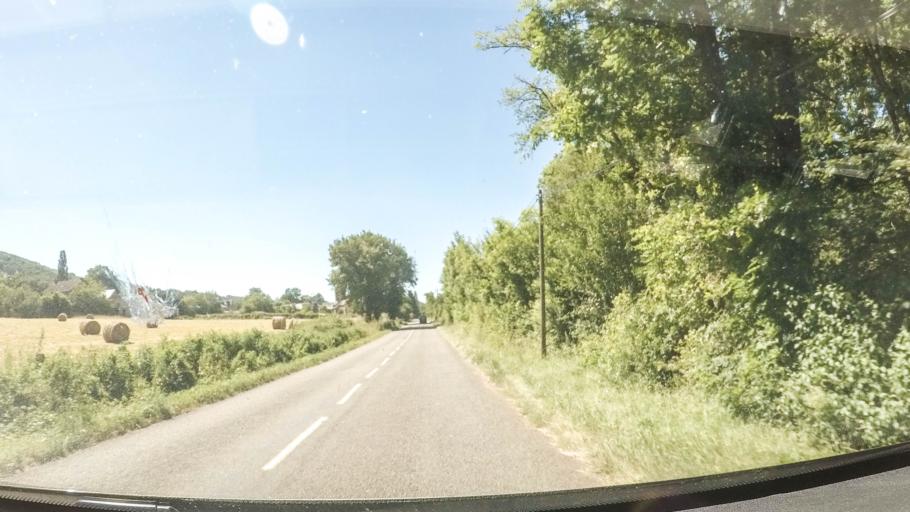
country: FR
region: Midi-Pyrenees
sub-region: Departement de l'Aveyron
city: Saint-Christophe-Vallon
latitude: 44.4621
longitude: 2.3909
